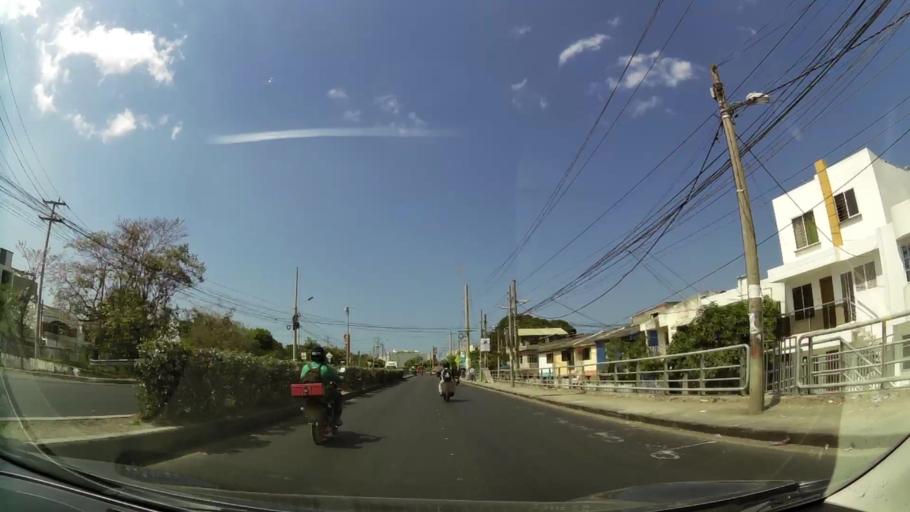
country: CO
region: Bolivar
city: Cartagena
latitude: 10.3798
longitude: -75.4633
